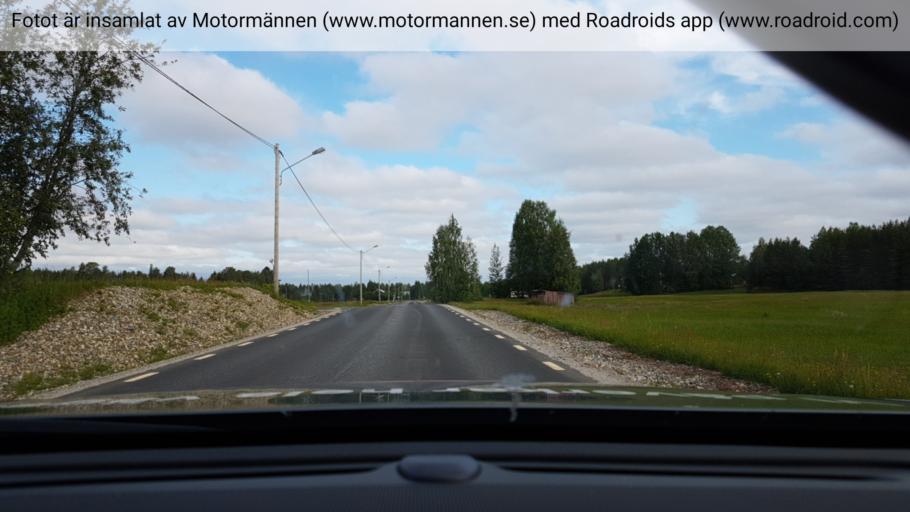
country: SE
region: Vaesterbotten
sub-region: Norsjo Kommun
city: Norsjoe
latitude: 64.5379
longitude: 19.3396
